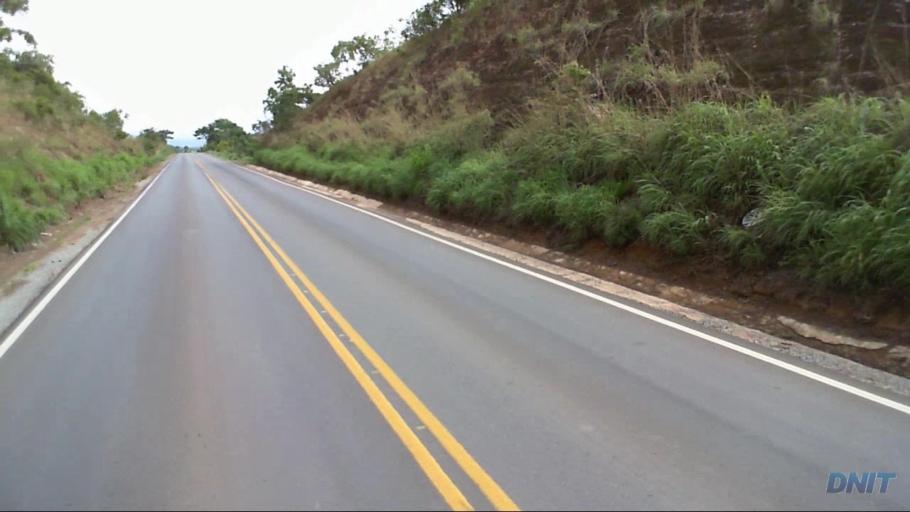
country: BR
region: Goias
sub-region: Padre Bernardo
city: Padre Bernardo
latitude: -15.2099
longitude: -48.2819
